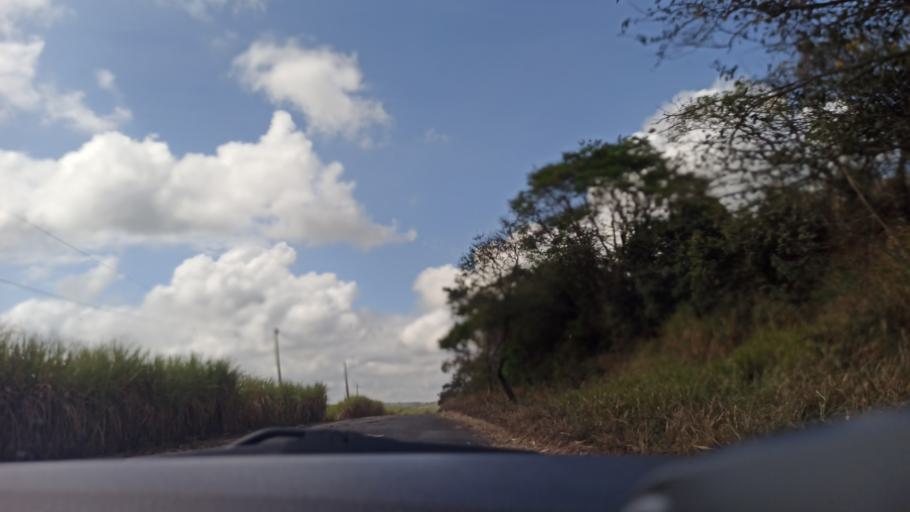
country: BR
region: Paraiba
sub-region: Juripiranga
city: Juripiranga
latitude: -7.3985
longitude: -35.2575
